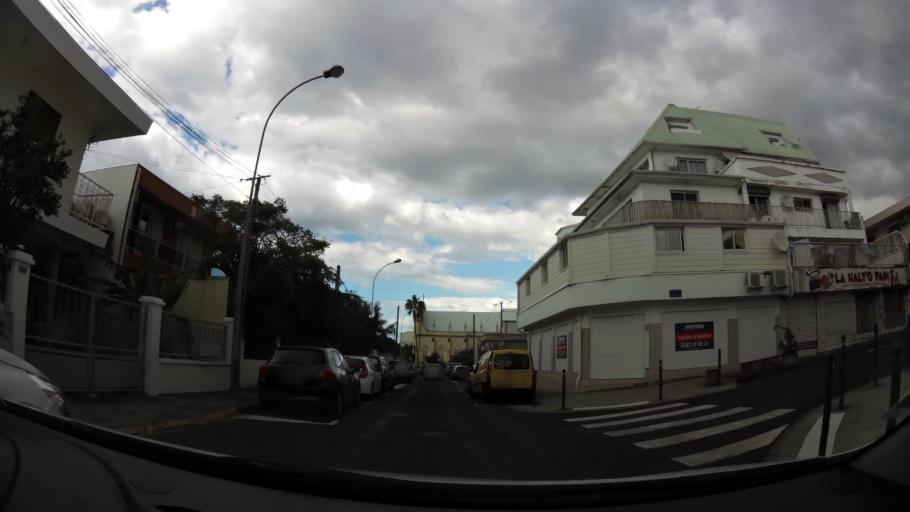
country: RE
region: Reunion
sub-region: Reunion
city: Saint-Denis
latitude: -20.8835
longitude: 55.4578
